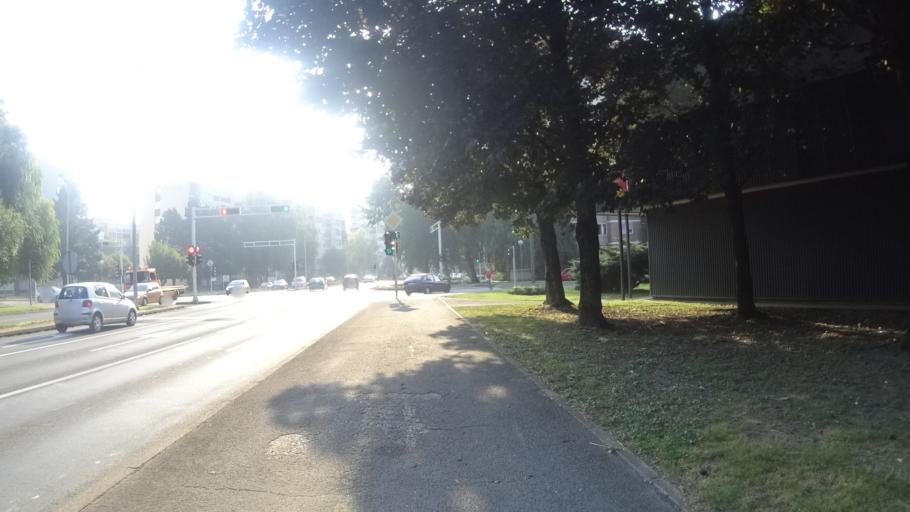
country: HR
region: Varazdinska
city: Varazdin
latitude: 46.3156
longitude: 16.3433
